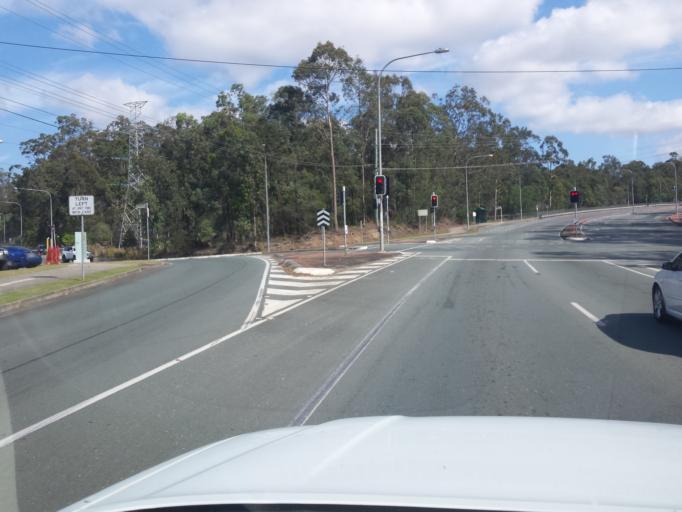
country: AU
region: Queensland
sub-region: Brisbane
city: Everton Park
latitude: -27.3808
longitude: 152.9816
